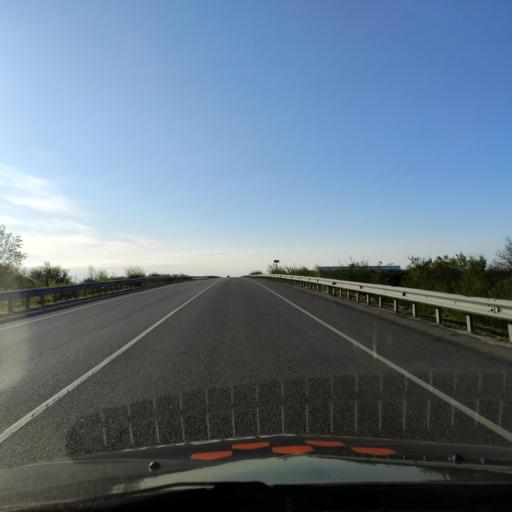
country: RU
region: Lipetsk
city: Yelets
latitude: 52.5654
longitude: 38.6747
